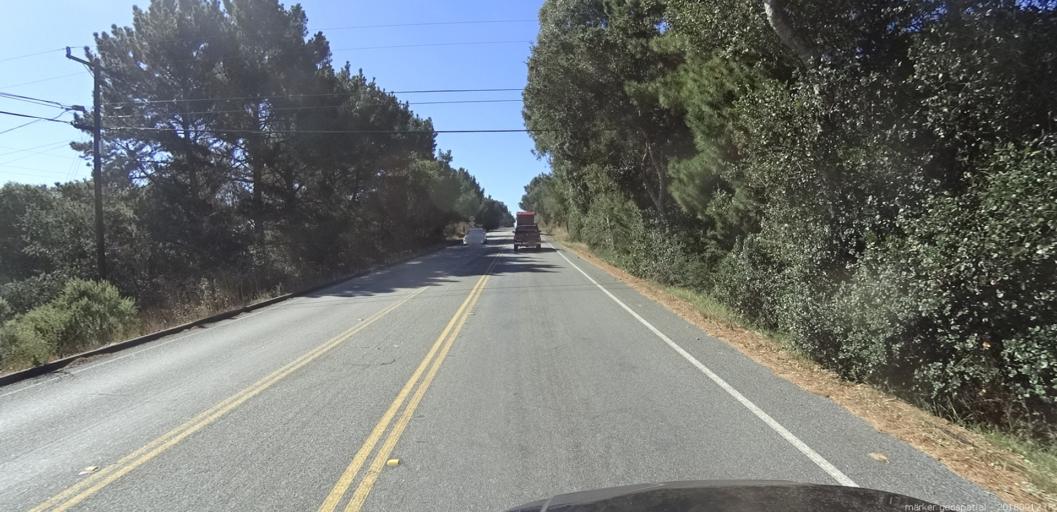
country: US
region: California
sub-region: Monterey County
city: Carmel Valley Village
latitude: 36.5445
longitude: -121.7535
